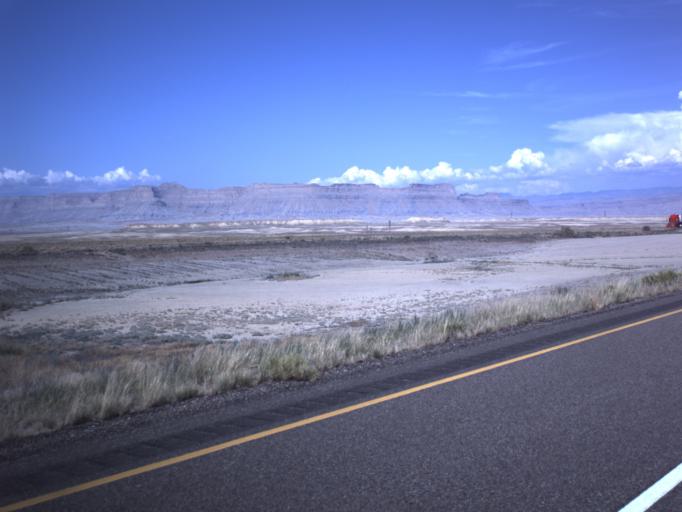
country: US
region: Utah
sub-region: Carbon County
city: East Carbon City
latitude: 38.9564
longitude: -110.3004
